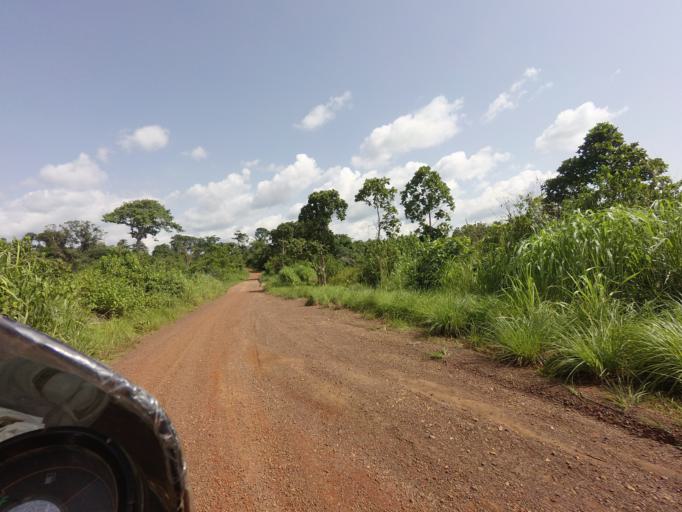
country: SL
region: Eastern Province
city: Daru
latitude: 8.0072
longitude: -10.8733
